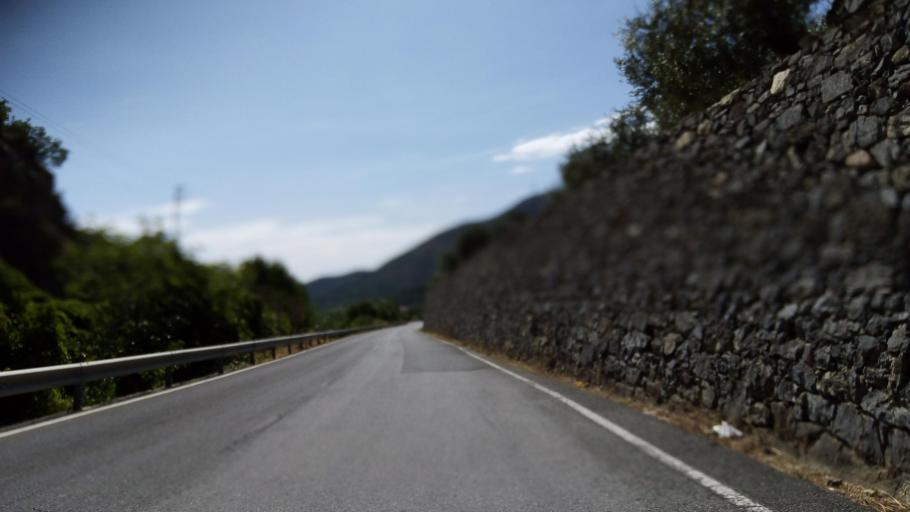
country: IT
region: Liguria
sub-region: Provincia di Savona
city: Toirano
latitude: 44.1344
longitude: 8.1995
